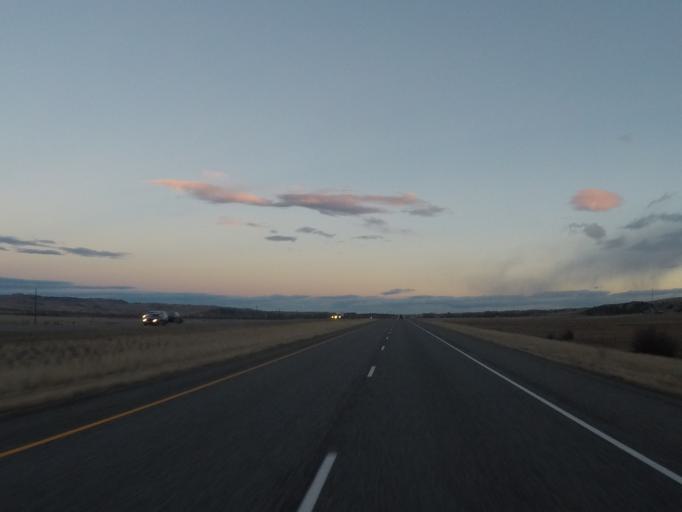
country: US
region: Montana
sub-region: Sweet Grass County
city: Big Timber
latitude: 45.7900
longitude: -109.8266
